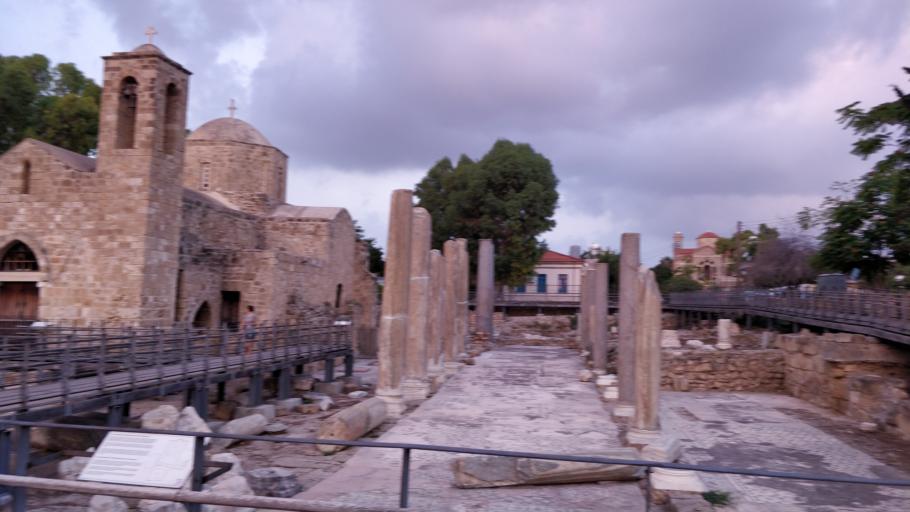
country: CY
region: Pafos
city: Paphos
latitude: 34.7577
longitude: 32.4138
